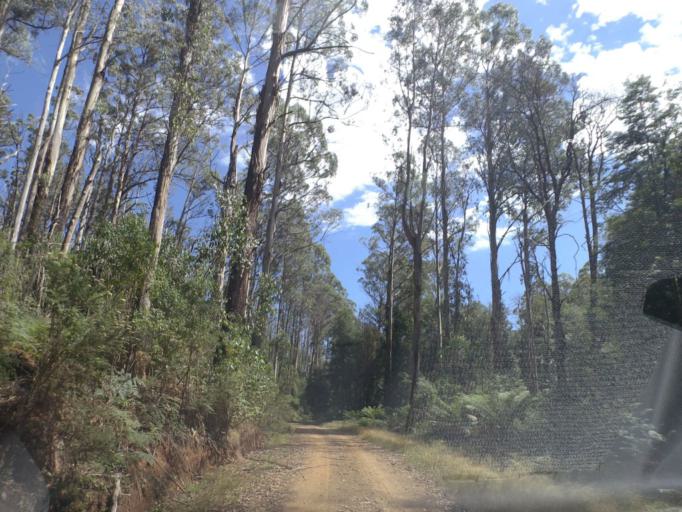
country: AU
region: Victoria
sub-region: Murrindindi
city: Alexandra
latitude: -37.4745
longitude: 145.8220
